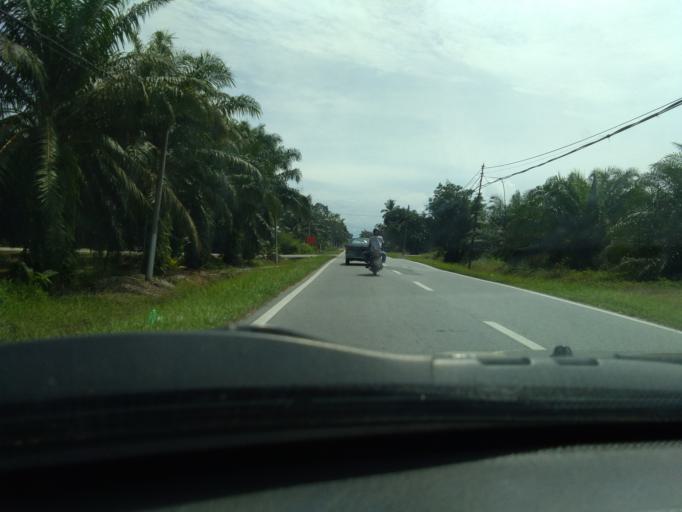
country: MY
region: Perak
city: Bagan Serai
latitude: 5.0303
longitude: 100.5601
